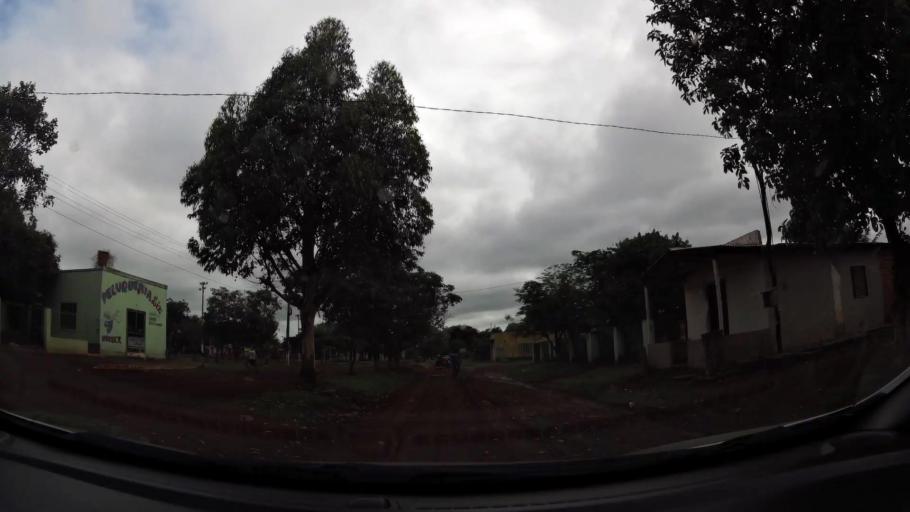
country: PY
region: Alto Parana
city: Ciudad del Este
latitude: -25.3722
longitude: -54.6482
